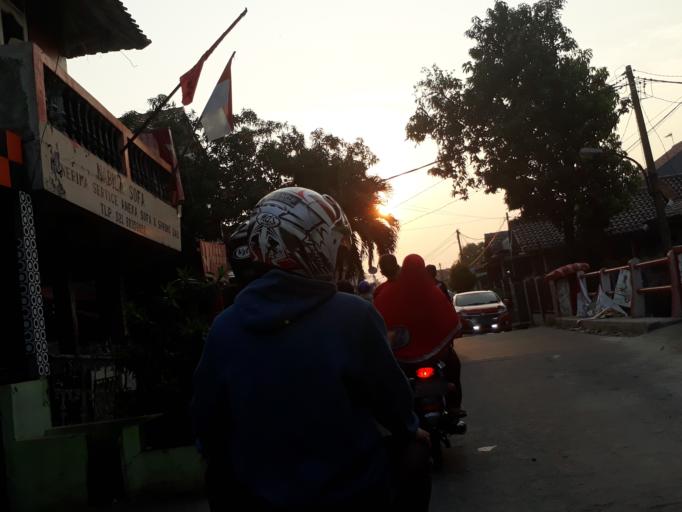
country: ID
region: West Java
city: Bekasi
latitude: -6.2422
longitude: 107.0397
